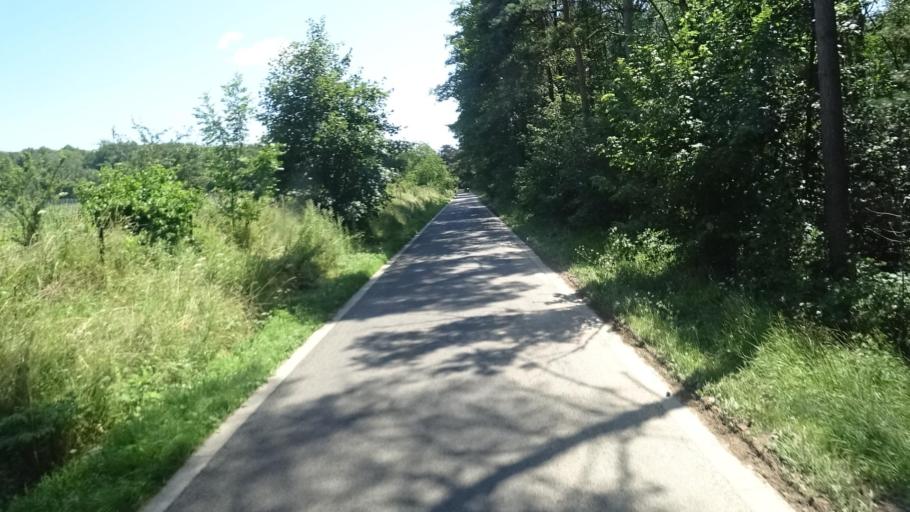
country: BE
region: Wallonia
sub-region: Province de Namur
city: Profondeville
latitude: 50.3536
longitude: 4.8320
